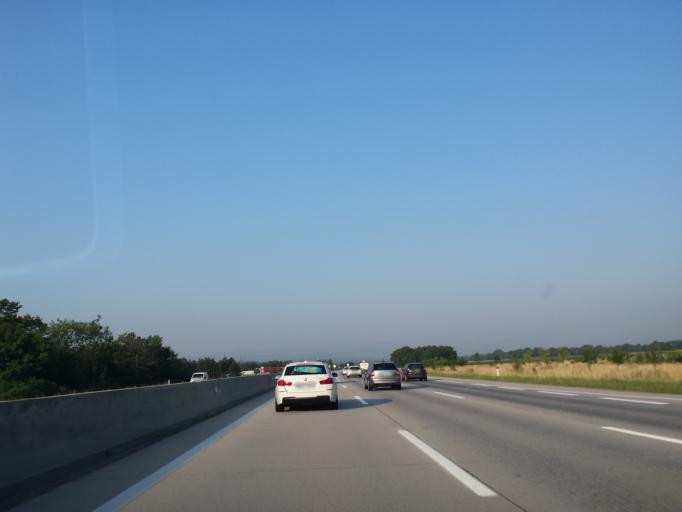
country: AT
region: Lower Austria
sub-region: Politischer Bezirk Wiener Neustadt
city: Bad Erlach
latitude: 47.7509
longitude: 16.1921
